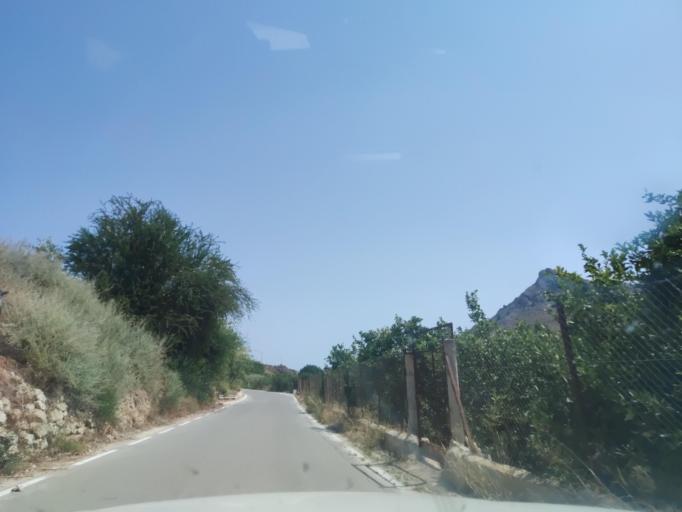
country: ES
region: Murcia
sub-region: Murcia
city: Ulea
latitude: 38.1345
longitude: -1.3161
